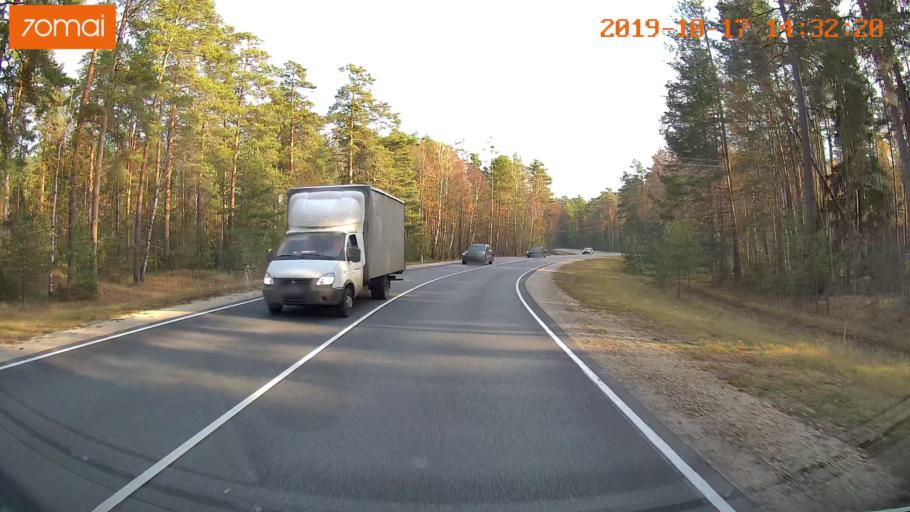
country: RU
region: Rjazan
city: Solotcha
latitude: 54.9285
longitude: 39.9777
